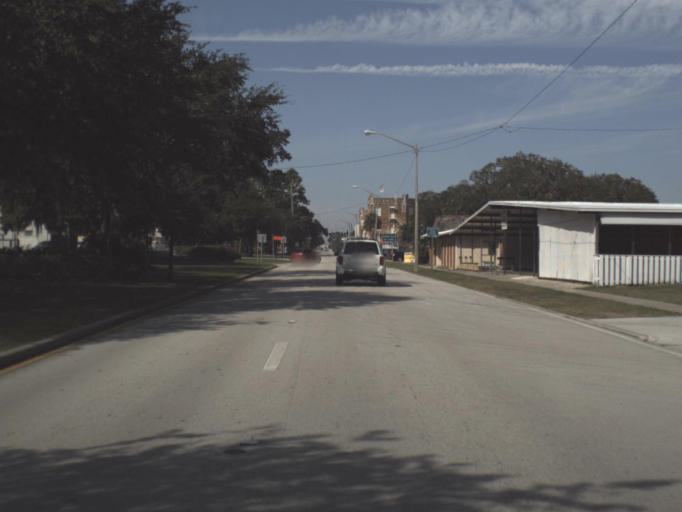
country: US
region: Florida
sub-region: Highlands County
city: Avon Park
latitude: 27.5959
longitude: -81.4991
